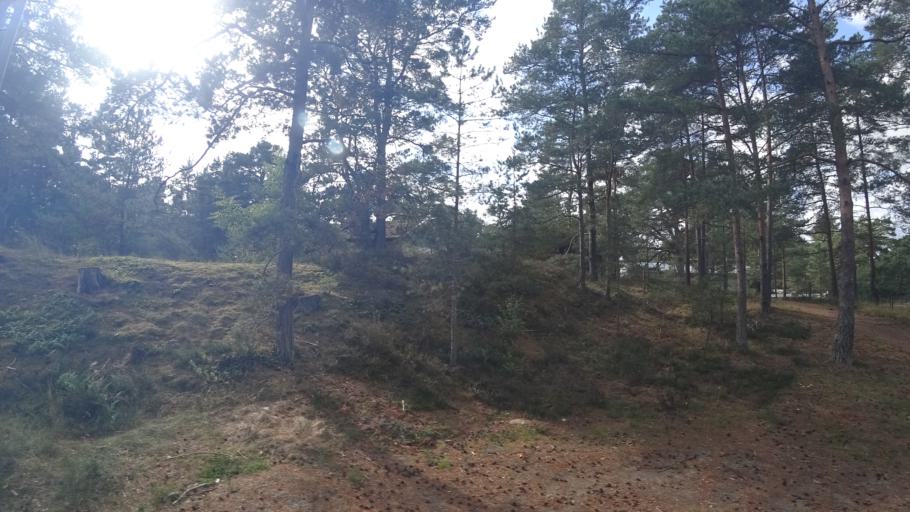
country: SE
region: Skane
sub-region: Kristianstads Kommun
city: Ahus
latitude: 55.9143
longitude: 14.2924
